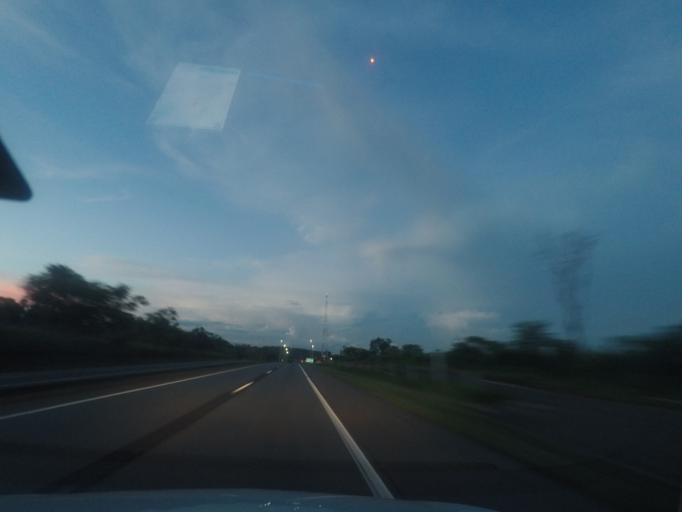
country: BR
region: Goias
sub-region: Piracanjuba
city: Piracanjuba
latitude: -17.4128
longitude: -49.2255
